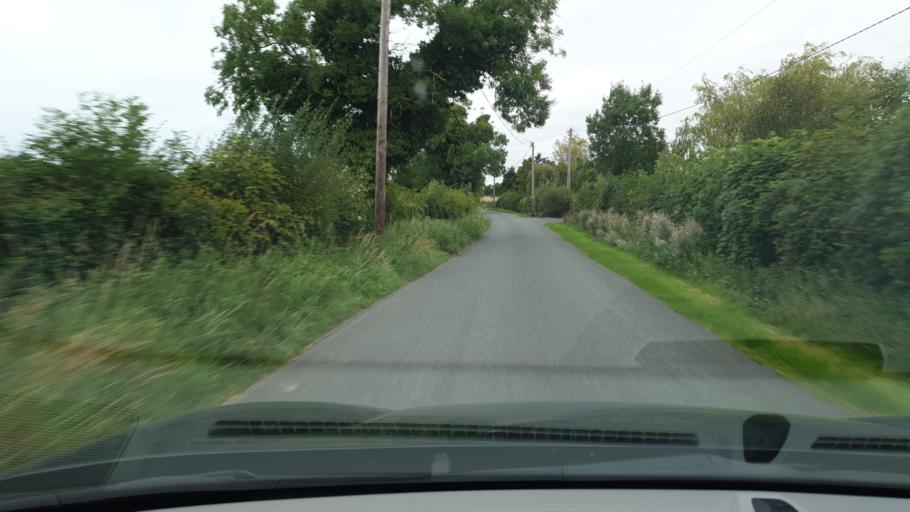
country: IE
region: Leinster
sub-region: An Mhi
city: Ratoath
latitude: 53.5081
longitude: -6.4871
